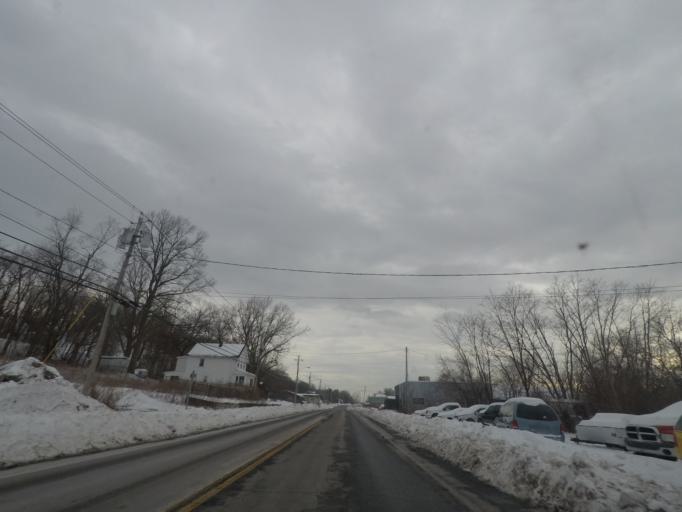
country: US
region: New York
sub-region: Rensselaer County
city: Hampton Manor
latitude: 42.6237
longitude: -73.7449
